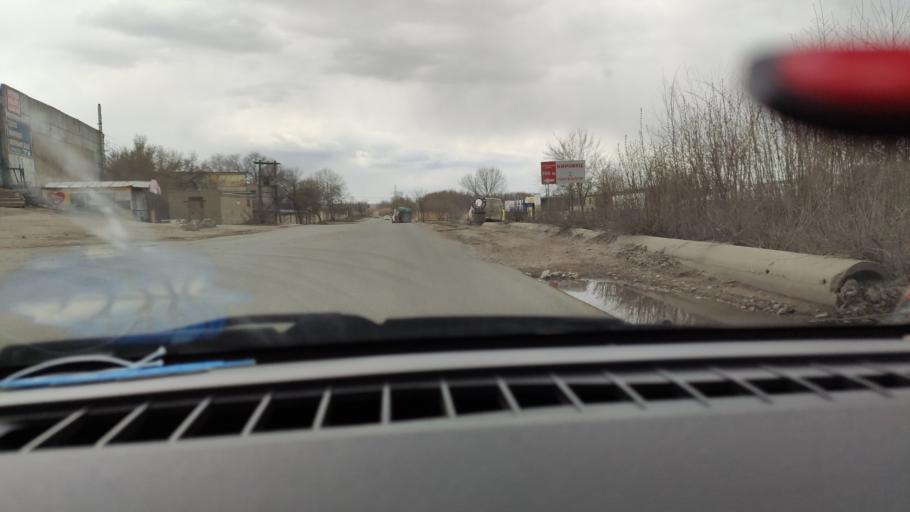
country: RU
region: Saratov
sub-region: Saratovskiy Rayon
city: Saratov
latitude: 51.6149
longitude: 45.9527
